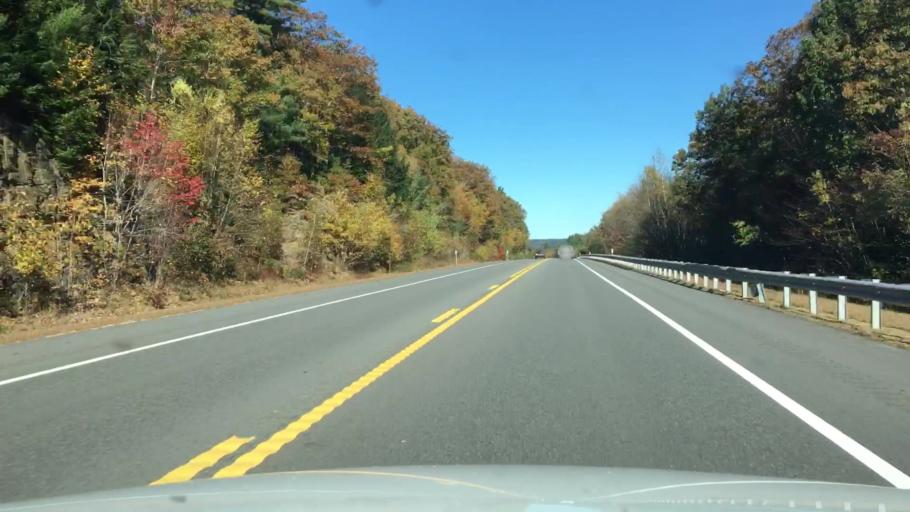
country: US
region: New Hampshire
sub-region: Strafford County
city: Rochester
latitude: 43.3646
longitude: -70.9874
